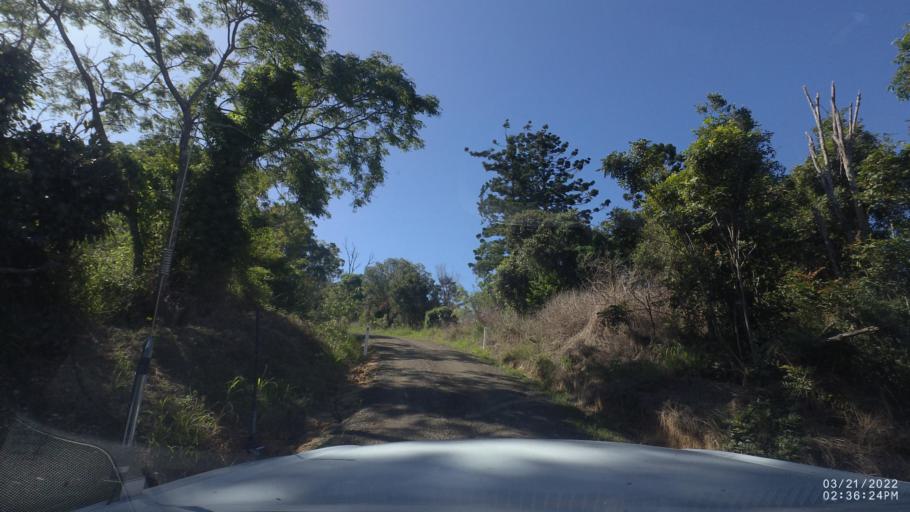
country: AU
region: Queensland
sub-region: Ipswich
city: Deebing Heights
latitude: -27.8258
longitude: 152.8155
